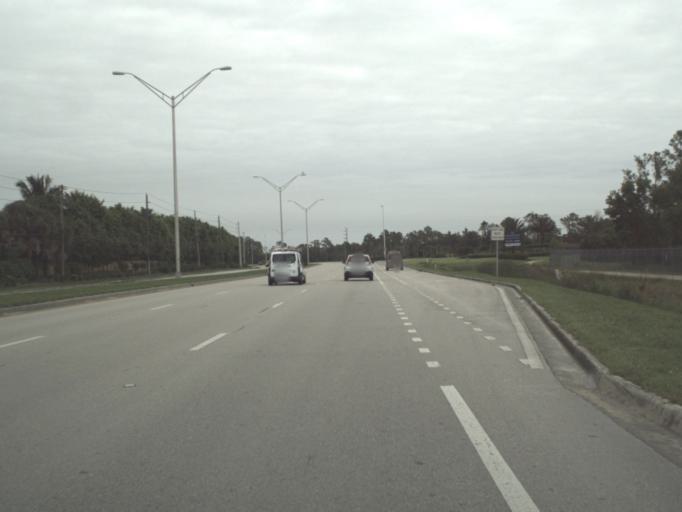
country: US
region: Florida
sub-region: Collier County
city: Lely Resort
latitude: 26.0749
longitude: -81.6901
